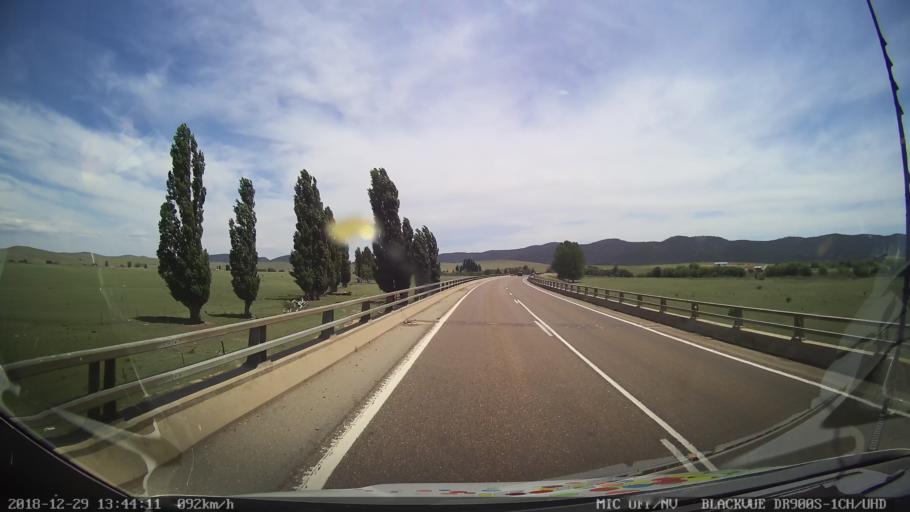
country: AU
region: New South Wales
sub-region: Cooma-Monaro
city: Cooma
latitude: -36.0819
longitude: 149.1561
